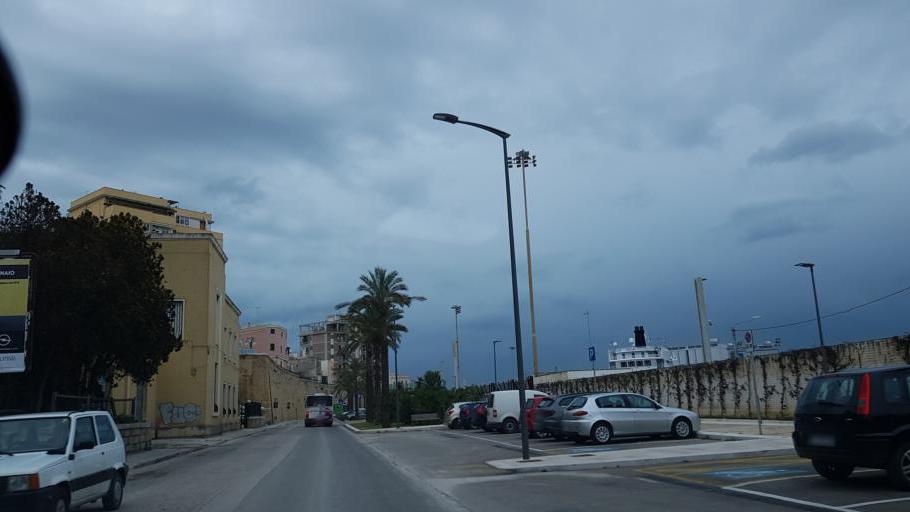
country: IT
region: Apulia
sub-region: Provincia di Brindisi
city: Brindisi
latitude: 40.6333
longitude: 17.9476
